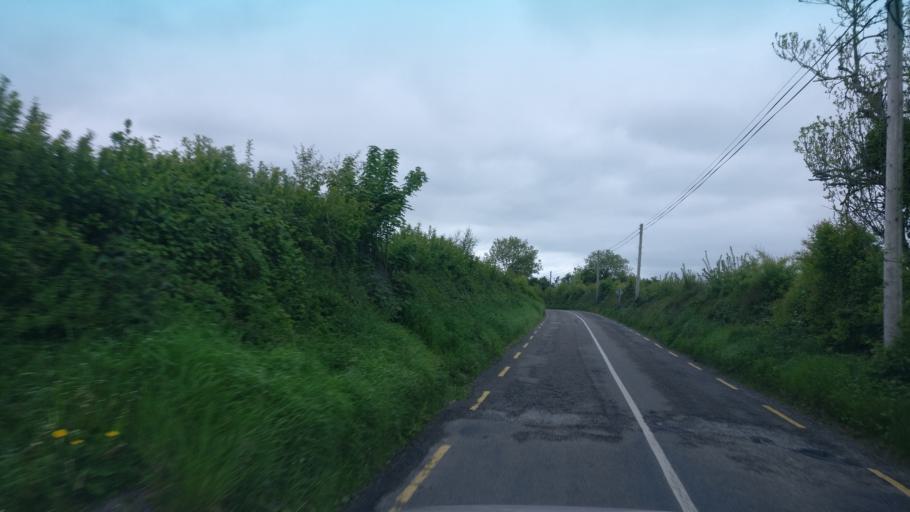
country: IE
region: Connaught
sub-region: County Galway
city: Portumna
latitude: 53.1046
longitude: -8.2578
